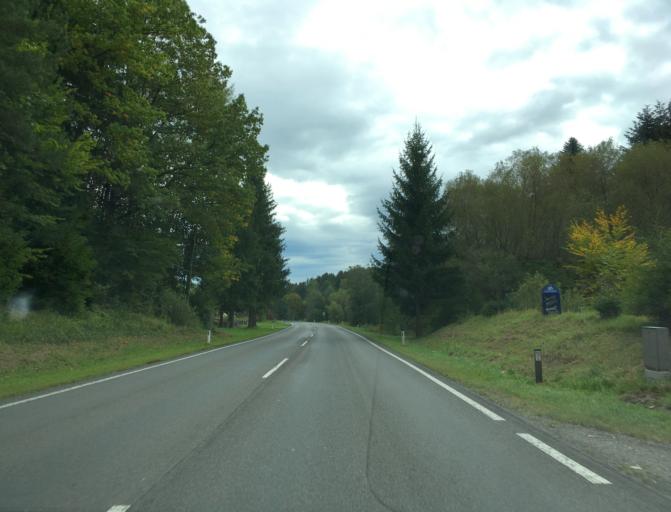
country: AT
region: Lower Austria
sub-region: Politischer Bezirk Neunkirchen
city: Thomasberg
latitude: 47.5344
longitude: 16.1713
